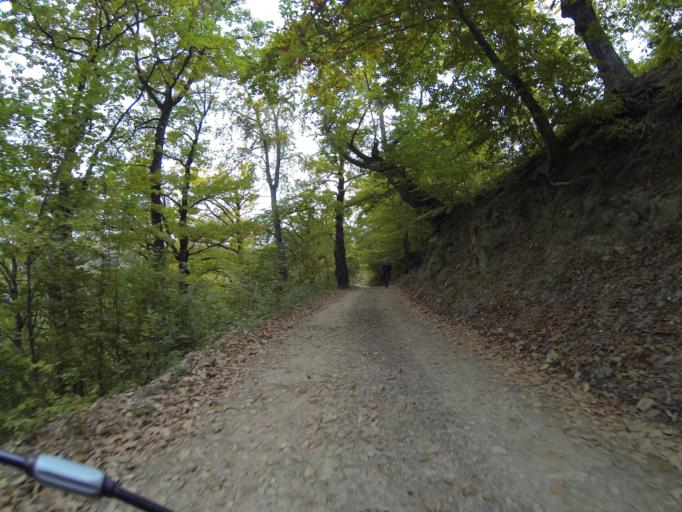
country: RO
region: Gorj
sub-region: Comuna Tismana
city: Sohodol
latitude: 45.0738
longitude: 22.8629
